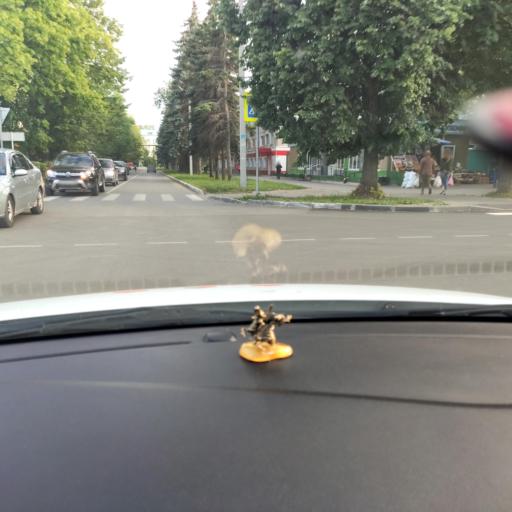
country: RU
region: Tatarstan
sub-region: Zelenodol'skiy Rayon
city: Zelenodolsk
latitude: 55.8490
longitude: 48.4983
